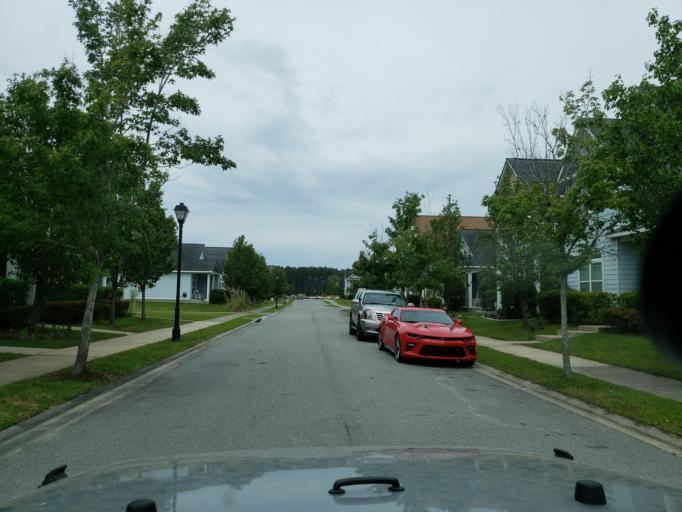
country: US
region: Georgia
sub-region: Chatham County
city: Port Wentworth
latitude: 32.2124
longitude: -81.1810
